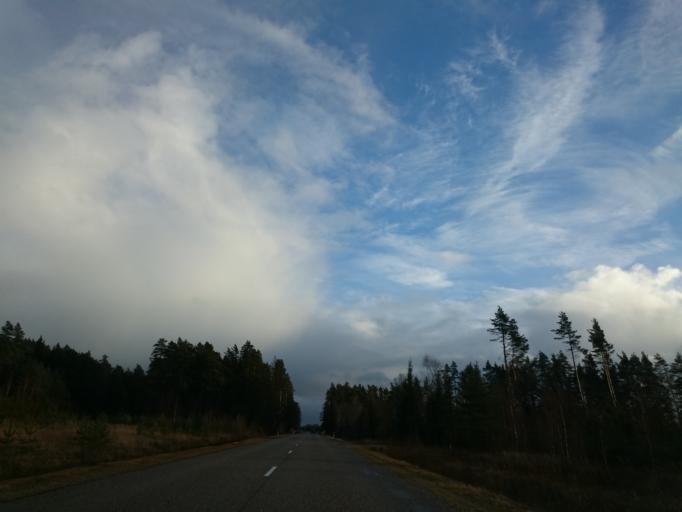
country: LV
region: Skrunda
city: Skrunda
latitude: 56.6801
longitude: 21.9544
